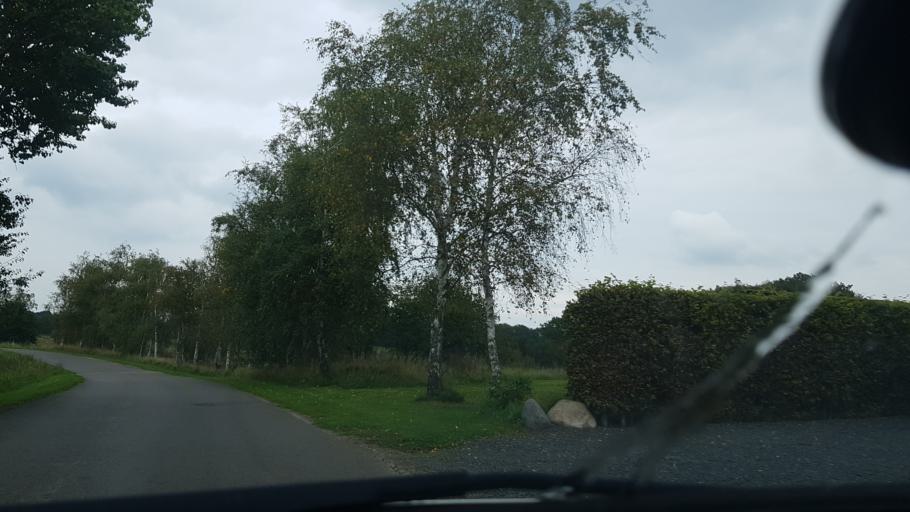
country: DK
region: South Denmark
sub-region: Kolding Kommune
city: Kolding
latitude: 55.5482
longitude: 9.3967
